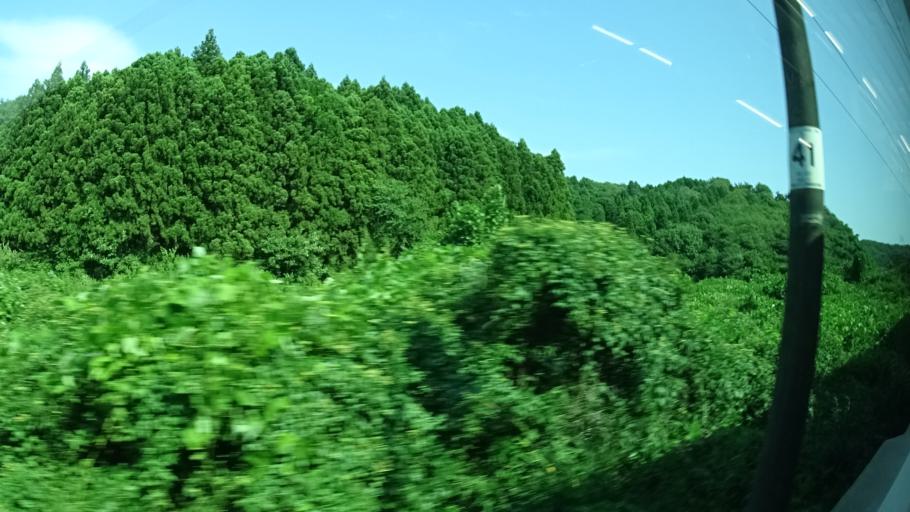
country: JP
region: Miyagi
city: Kogota
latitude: 38.4935
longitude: 141.0881
